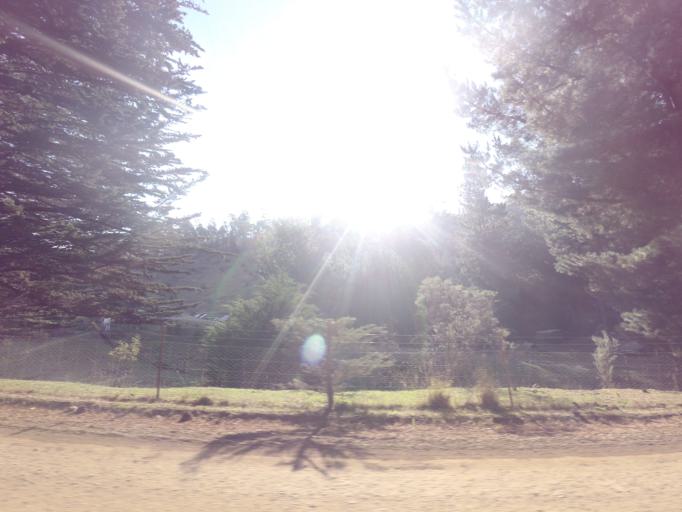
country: AU
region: Tasmania
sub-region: Sorell
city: Sorell
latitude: -42.4881
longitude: 147.4343
